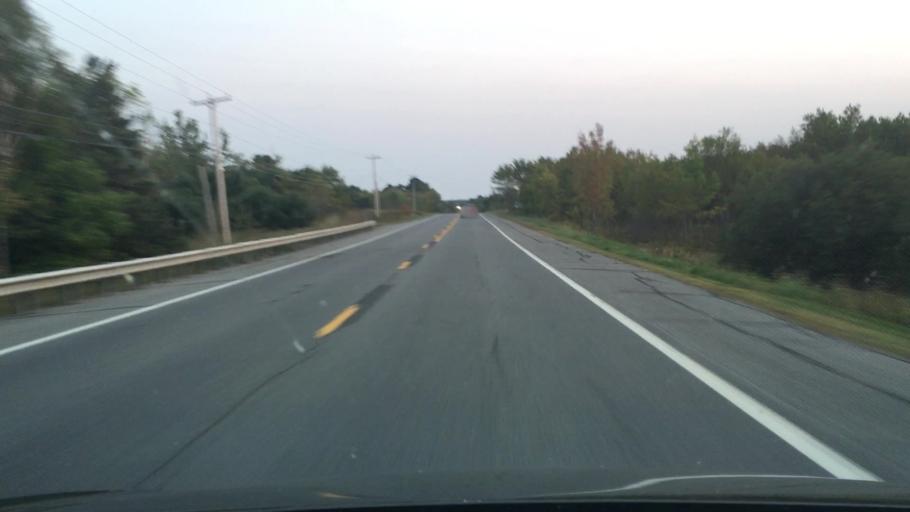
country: US
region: Maine
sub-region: Waldo County
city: Stockton Springs
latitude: 44.5344
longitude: -68.8612
